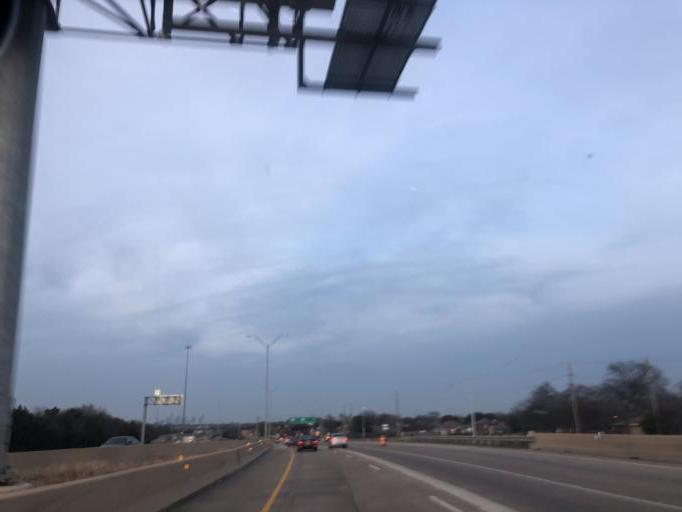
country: US
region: Texas
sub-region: Dallas County
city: Cockrell Hill
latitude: 32.6848
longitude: -96.8496
